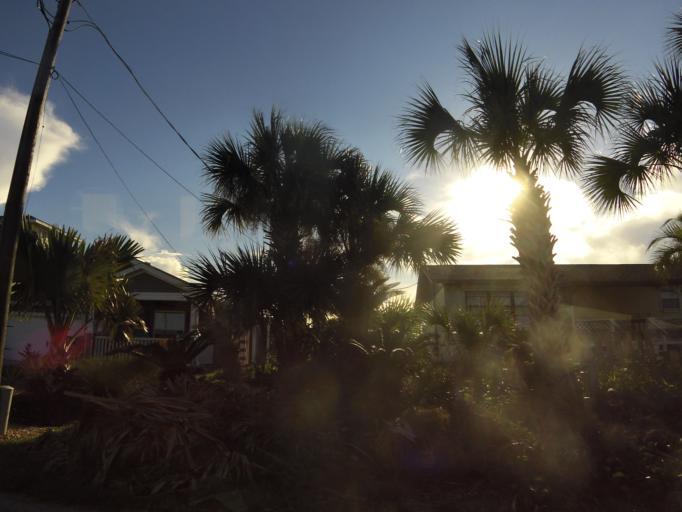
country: US
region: Florida
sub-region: Flagler County
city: Flagler Beach
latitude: 29.4605
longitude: -81.1187
